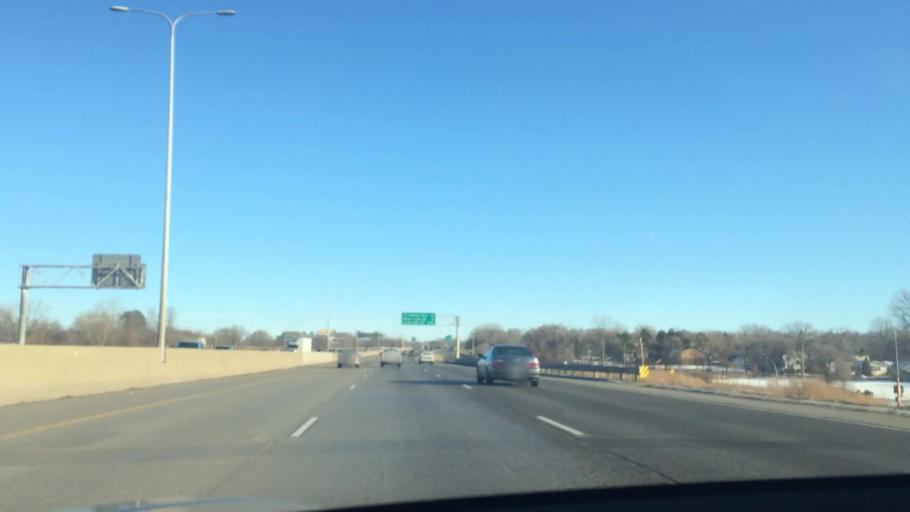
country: US
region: Minnesota
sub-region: Anoka County
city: Fridley
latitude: 45.0683
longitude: -93.2648
